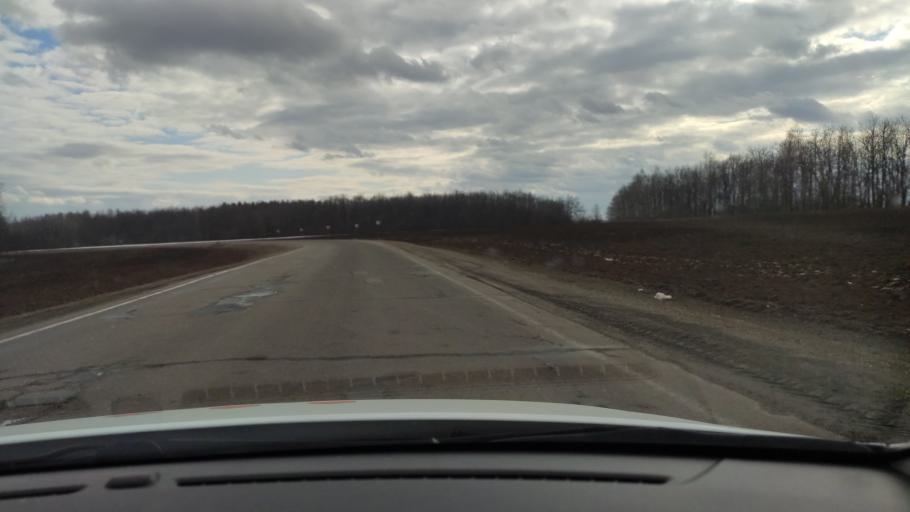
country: RU
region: Tatarstan
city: Vysokaya Gora
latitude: 56.0878
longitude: 49.1816
